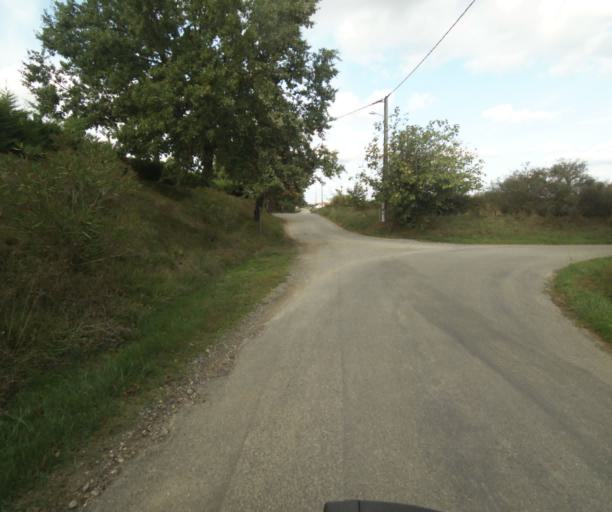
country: FR
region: Midi-Pyrenees
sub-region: Departement du Tarn-et-Garonne
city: Verdun-sur-Garonne
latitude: 43.8417
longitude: 1.1217
